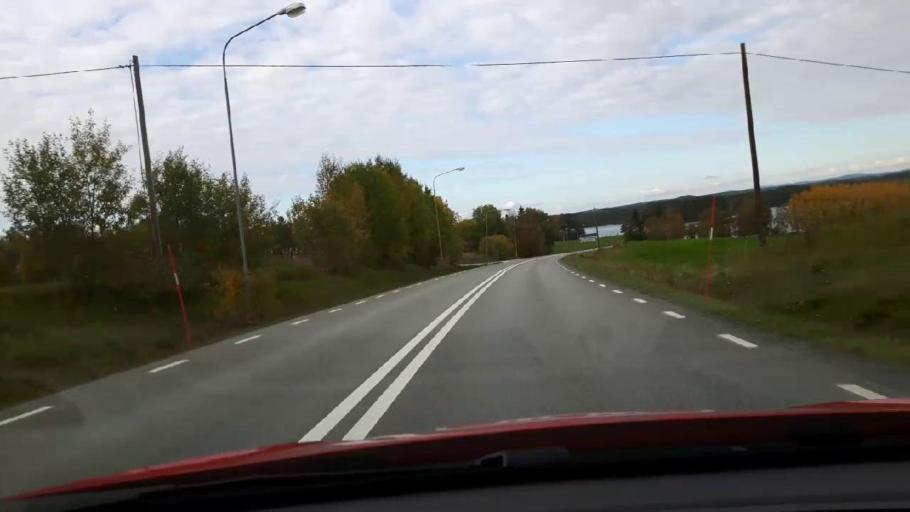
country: SE
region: Jaemtland
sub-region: Krokoms Kommun
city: Valla
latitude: 63.2410
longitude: 14.0013
